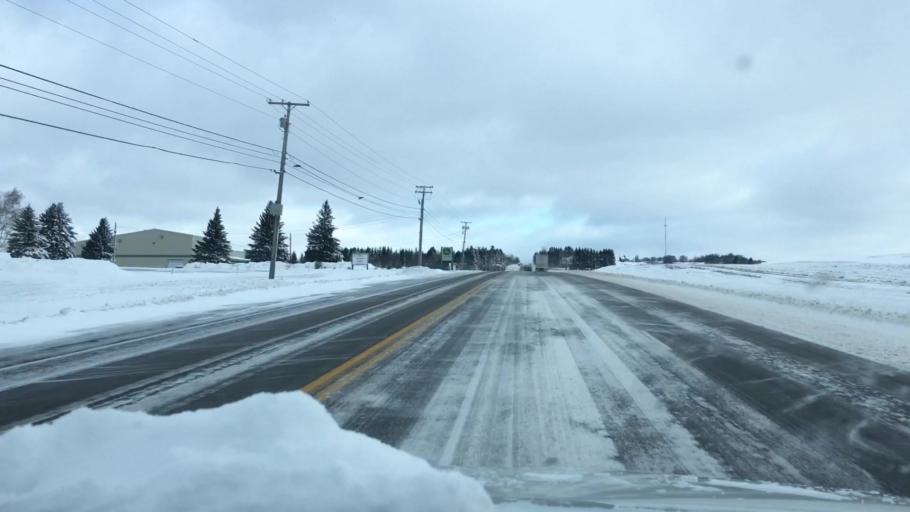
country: US
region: Maine
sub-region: Aroostook County
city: Presque Isle
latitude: 46.7183
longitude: -68.0077
